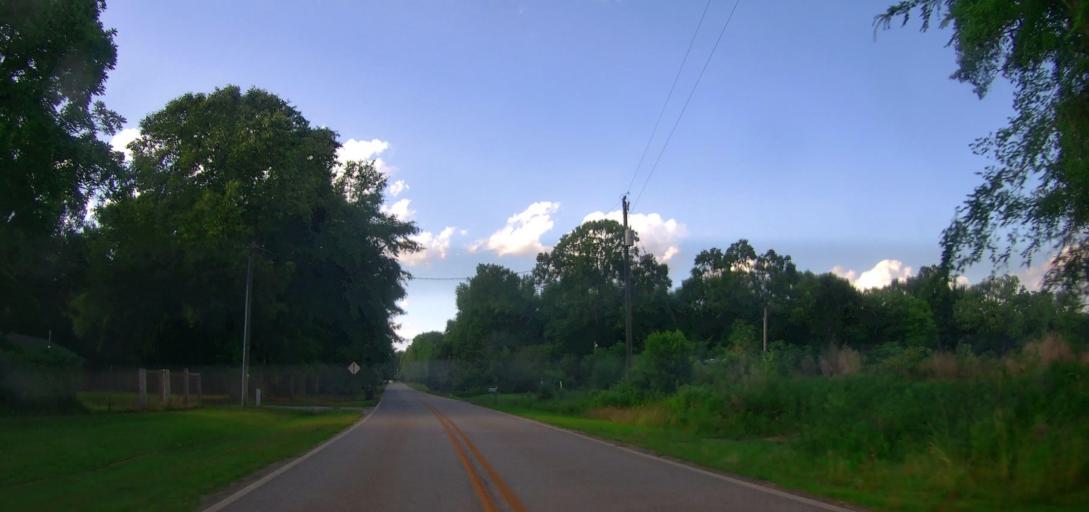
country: US
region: Georgia
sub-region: Peach County
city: Byron
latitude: 32.6565
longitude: -83.7913
